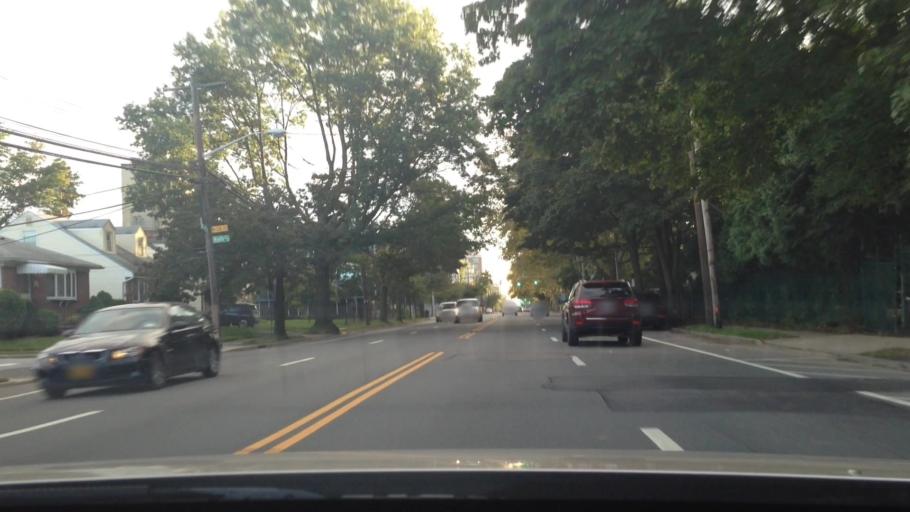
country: US
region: New York
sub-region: Nassau County
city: Mineola
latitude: 40.7375
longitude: -73.6469
